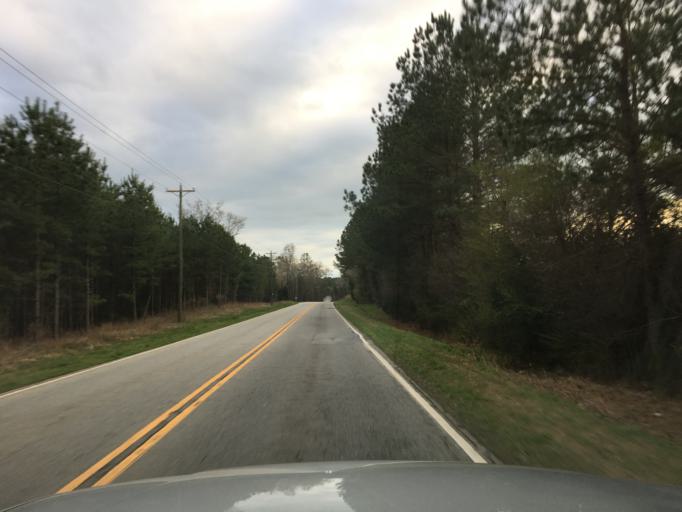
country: US
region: South Carolina
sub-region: Saluda County
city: Saluda
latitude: 33.9802
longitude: -81.7710
